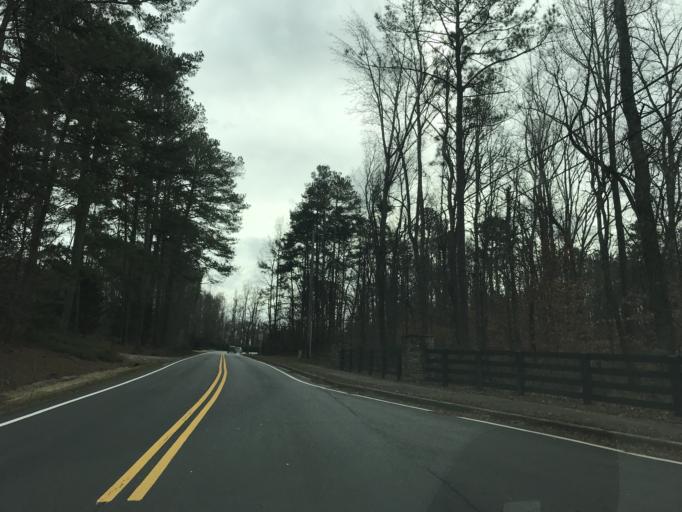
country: US
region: Georgia
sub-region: Fulton County
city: Milton
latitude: 34.1409
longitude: -84.2863
